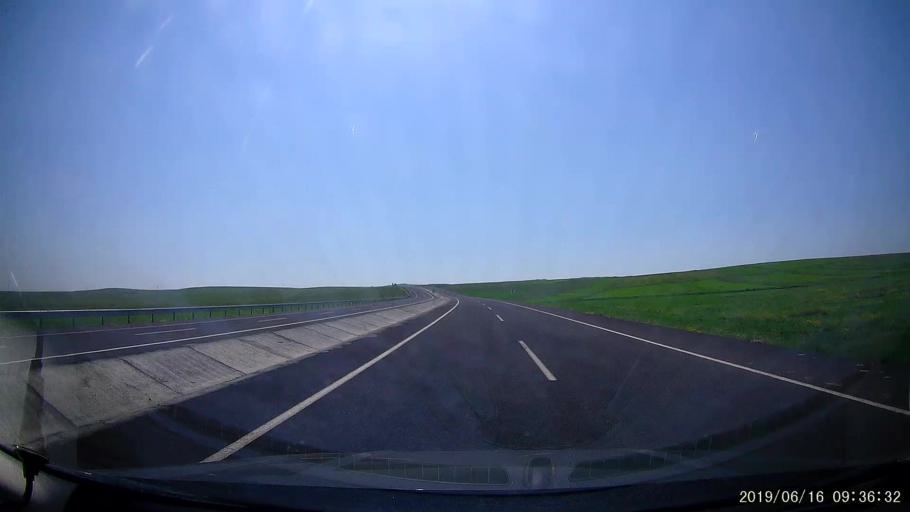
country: TR
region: Kars
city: Kars
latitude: 40.5572
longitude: 43.1744
